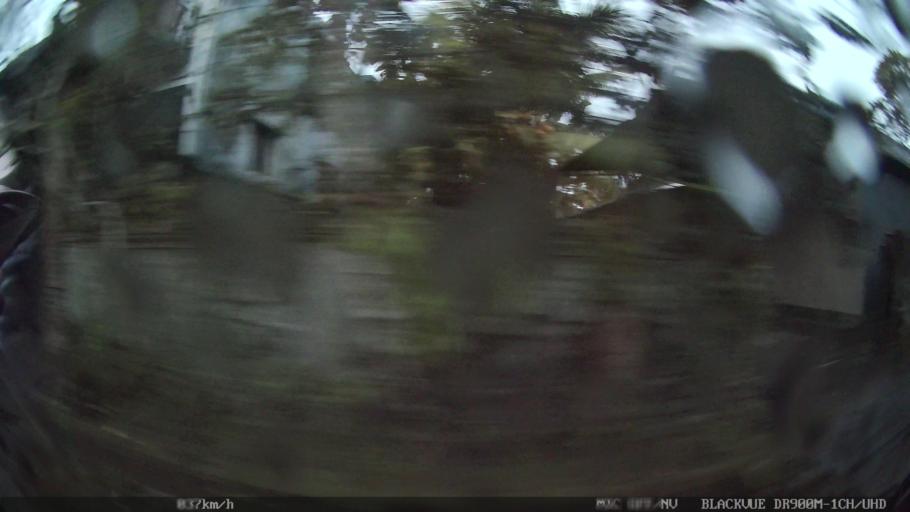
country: ID
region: Bali
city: Banjar Sedang
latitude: -8.5629
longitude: 115.2520
